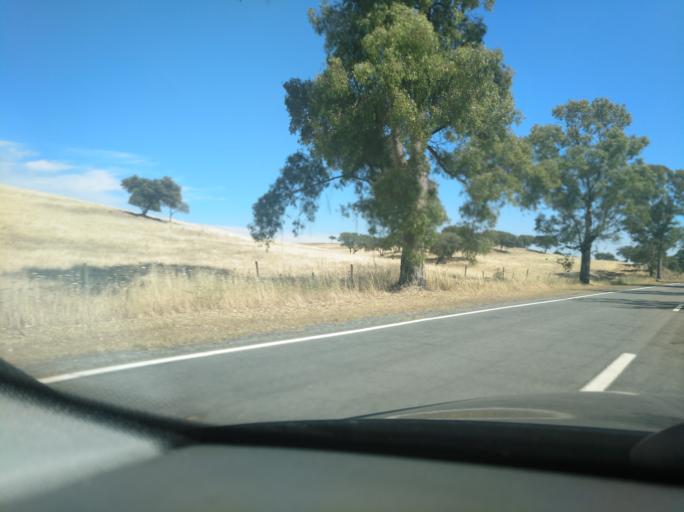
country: PT
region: Beja
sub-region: Castro Verde
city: Castro Verde
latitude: 37.6739
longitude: -8.0821
